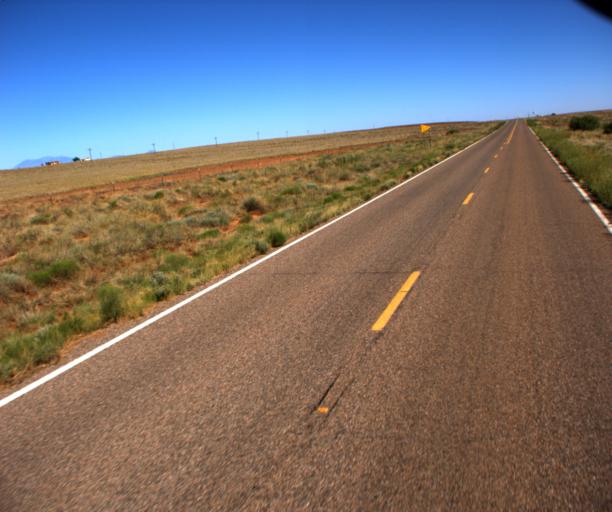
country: US
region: Arizona
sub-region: Coconino County
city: LeChee
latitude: 35.1682
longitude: -110.9155
